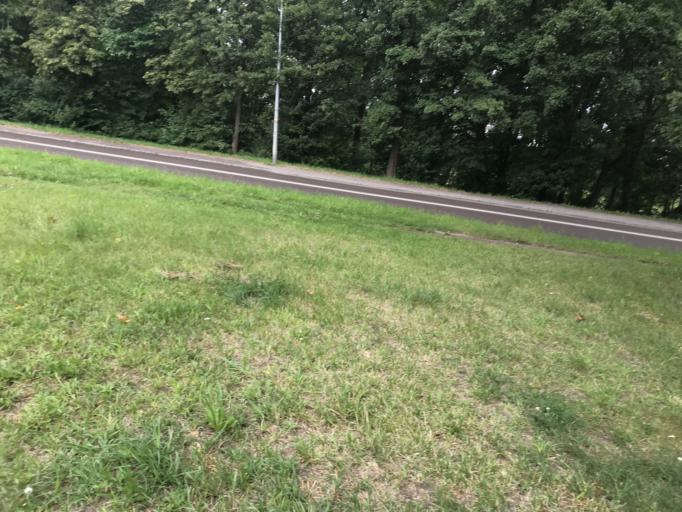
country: PL
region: Warmian-Masurian Voivodeship
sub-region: Powiat elblaski
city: Elblag
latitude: 54.1729
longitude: 19.4245
